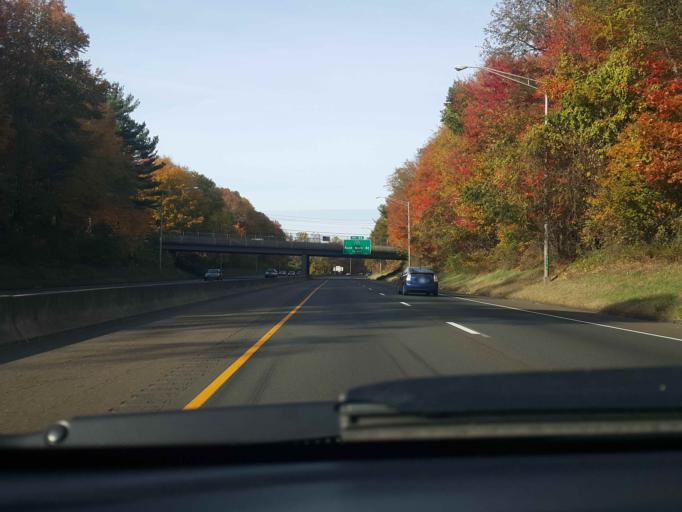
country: US
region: Connecticut
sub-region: New Haven County
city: North Branford
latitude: 41.2941
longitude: -72.7746
